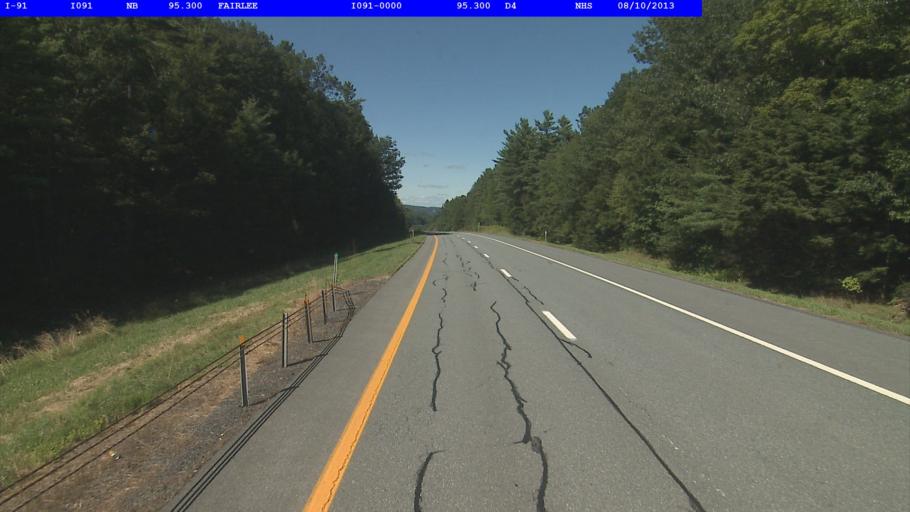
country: US
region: New Hampshire
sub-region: Grafton County
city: Orford
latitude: 43.9517
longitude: -72.1300
